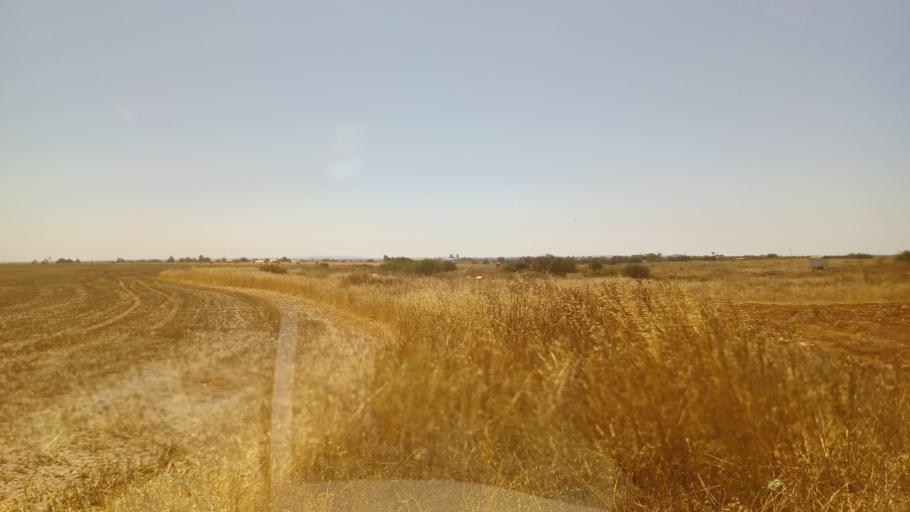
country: CY
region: Larnaka
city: Pergamos
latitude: 35.0239
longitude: 33.7174
